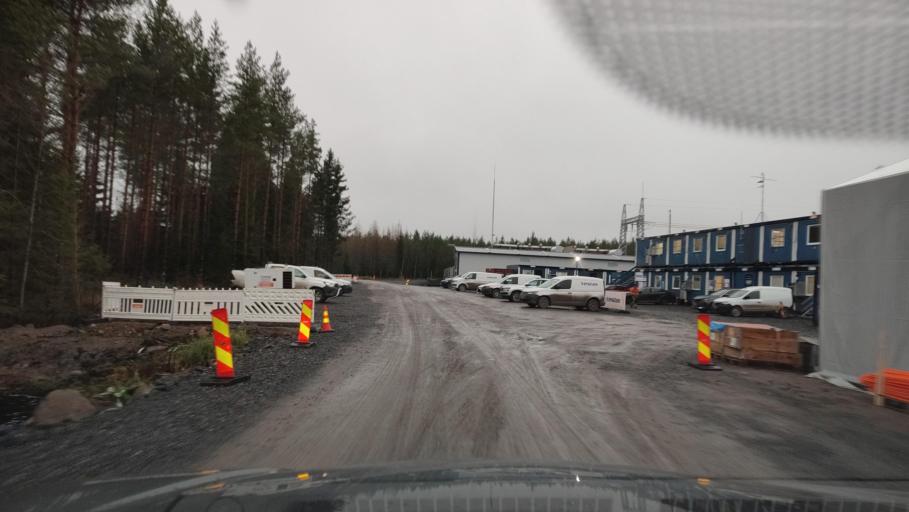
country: FI
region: Southern Ostrobothnia
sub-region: Suupohja
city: Karijoki
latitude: 62.1812
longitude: 21.5900
